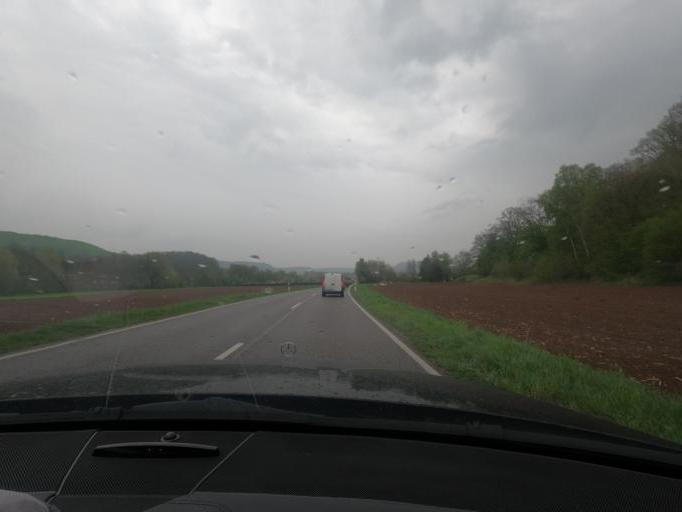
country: DE
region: Thuringia
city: Burgwalde
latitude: 51.3684
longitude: 10.0567
